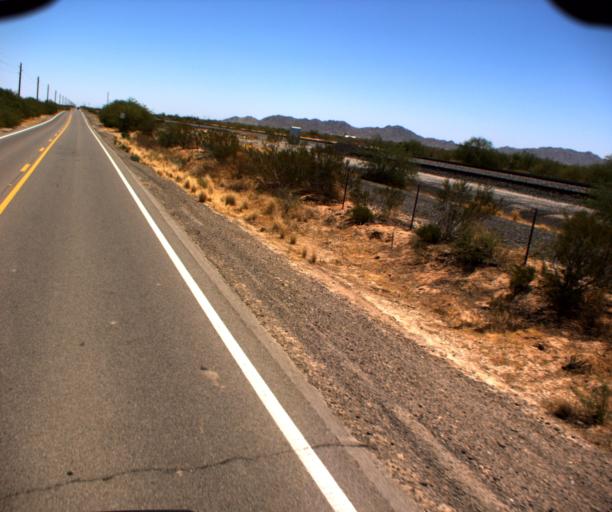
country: US
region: Arizona
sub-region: Pinal County
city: Maricopa
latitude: 33.0608
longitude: -112.2505
